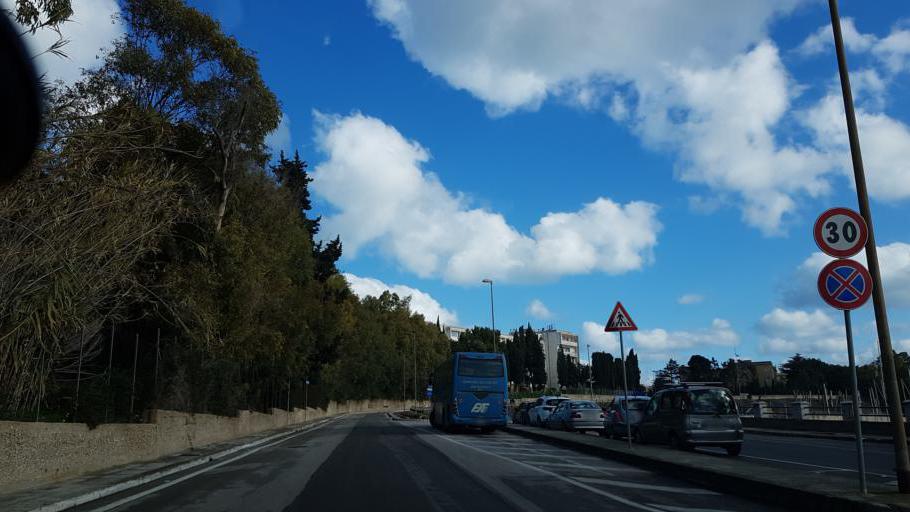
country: IT
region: Apulia
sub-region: Provincia di Brindisi
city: Brindisi
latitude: 40.6431
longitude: 17.9350
